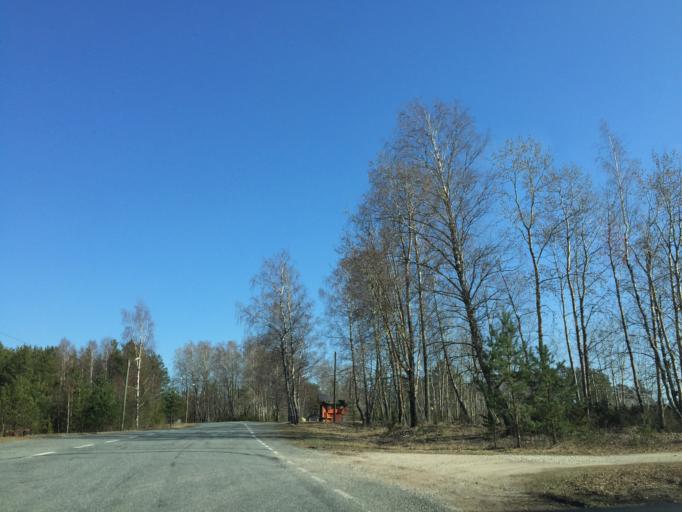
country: EE
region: Ida-Virumaa
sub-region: Johvi vald
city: Johvi
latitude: 59.0031
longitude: 27.3349
